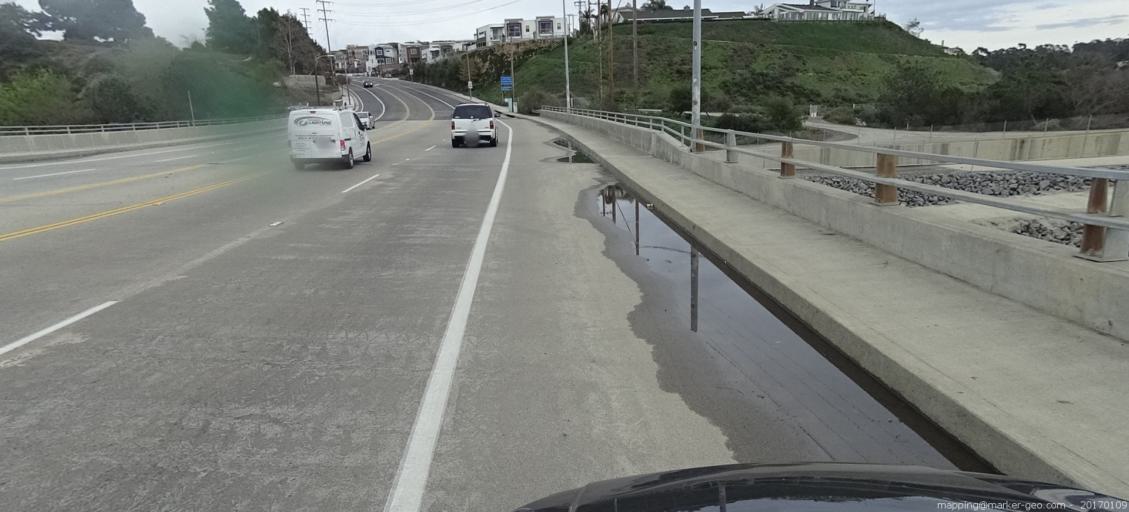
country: US
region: California
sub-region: Orange County
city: Costa Mesa
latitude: 33.6506
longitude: -117.9511
